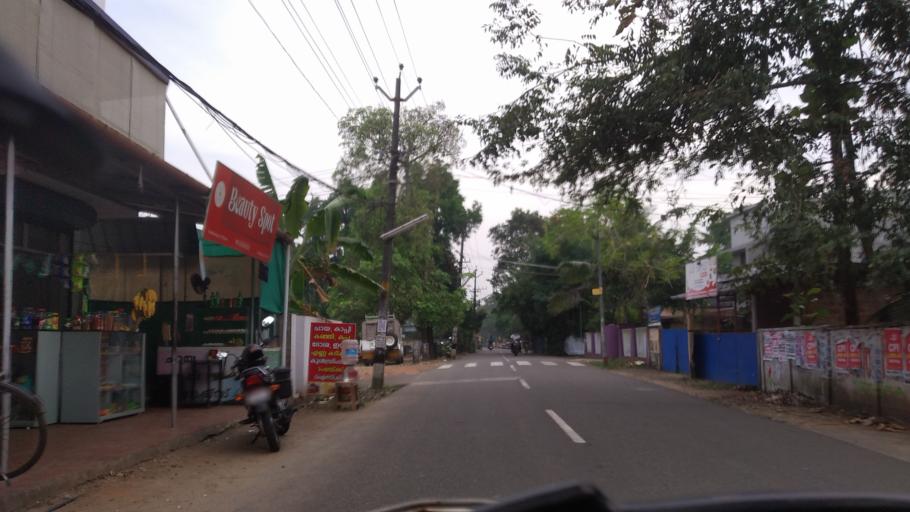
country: IN
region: Kerala
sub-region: Ernakulam
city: Elur
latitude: 10.1440
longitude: 76.2469
